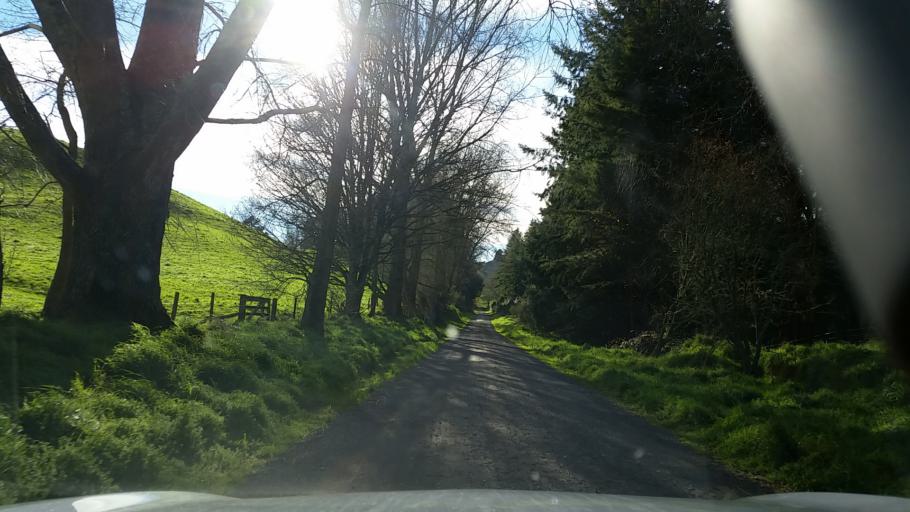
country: NZ
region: Waikato
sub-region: South Waikato District
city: Tokoroa
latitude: -38.3822
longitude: 176.0822
